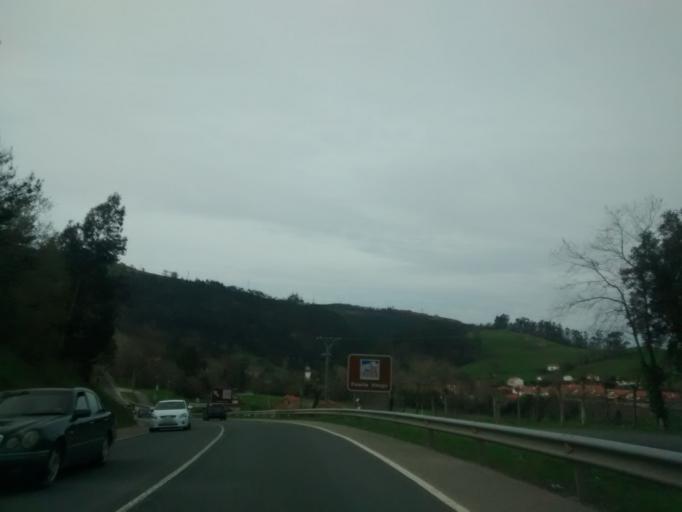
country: ES
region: Cantabria
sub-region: Provincia de Cantabria
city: Puente Viesgo
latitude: 43.2927
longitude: -3.9623
